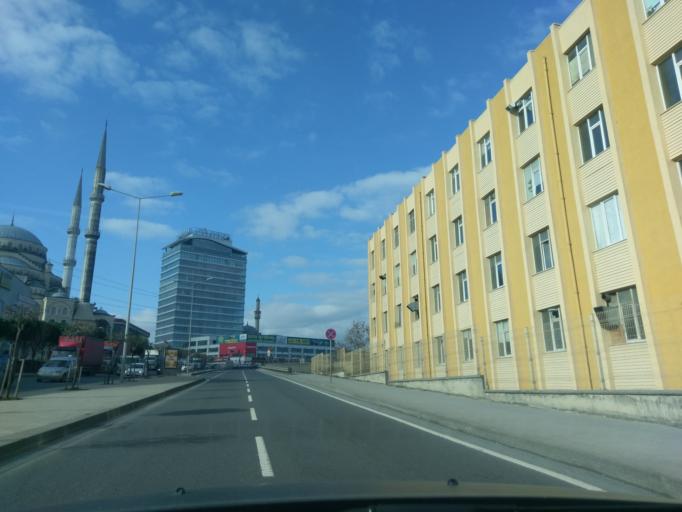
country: TR
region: Istanbul
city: Basaksehir
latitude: 41.0699
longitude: 28.8075
